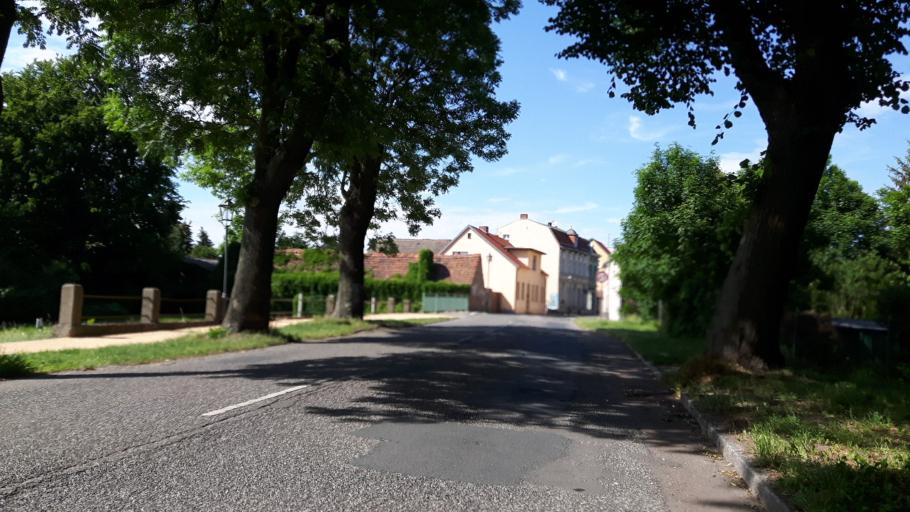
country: DE
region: Brandenburg
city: Beelitz
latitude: 52.2309
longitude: 12.9746
